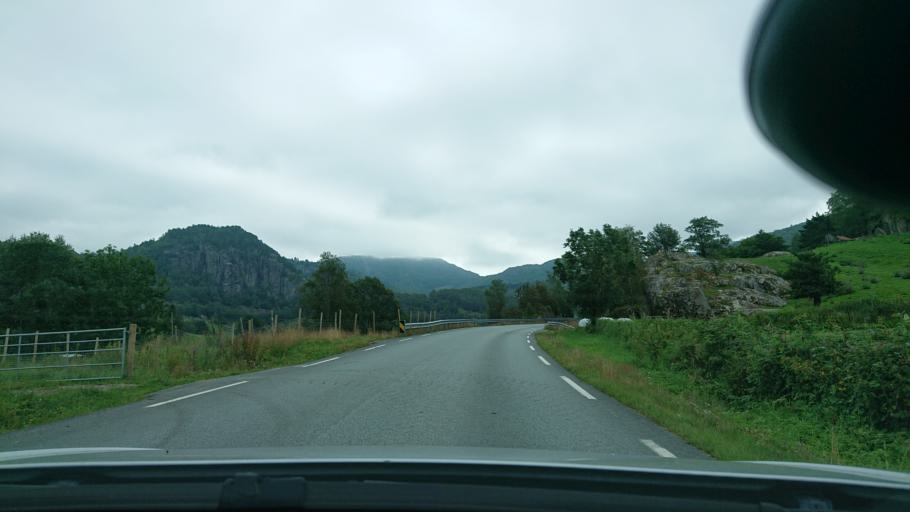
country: NO
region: Rogaland
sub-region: Hjelmeland
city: Hjelmelandsvagen
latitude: 59.2256
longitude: 6.2092
